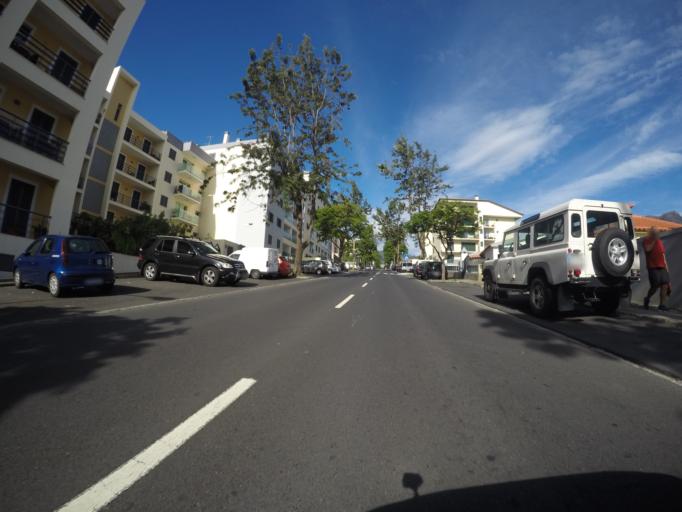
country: PT
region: Madeira
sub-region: Funchal
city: Nossa Senhora do Monte
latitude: 32.6566
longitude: -16.9250
